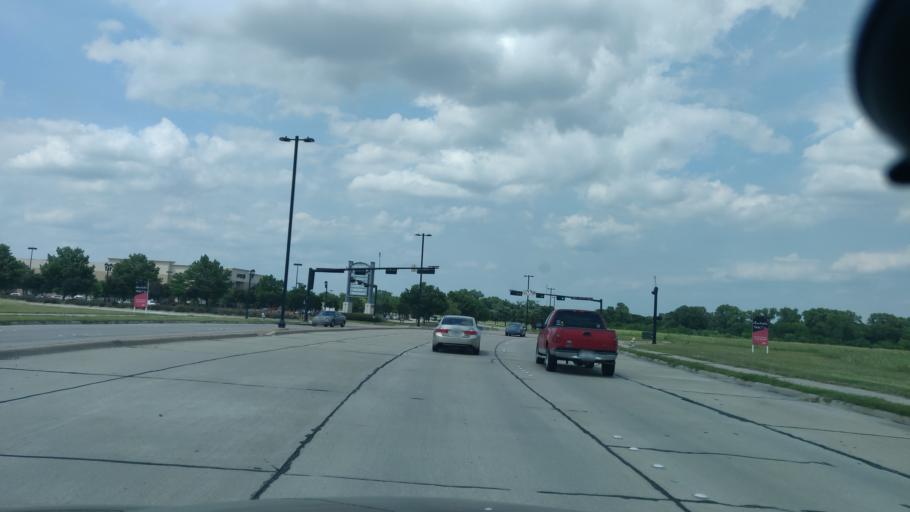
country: US
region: Texas
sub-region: Dallas County
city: Sachse
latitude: 32.9495
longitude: -96.6092
